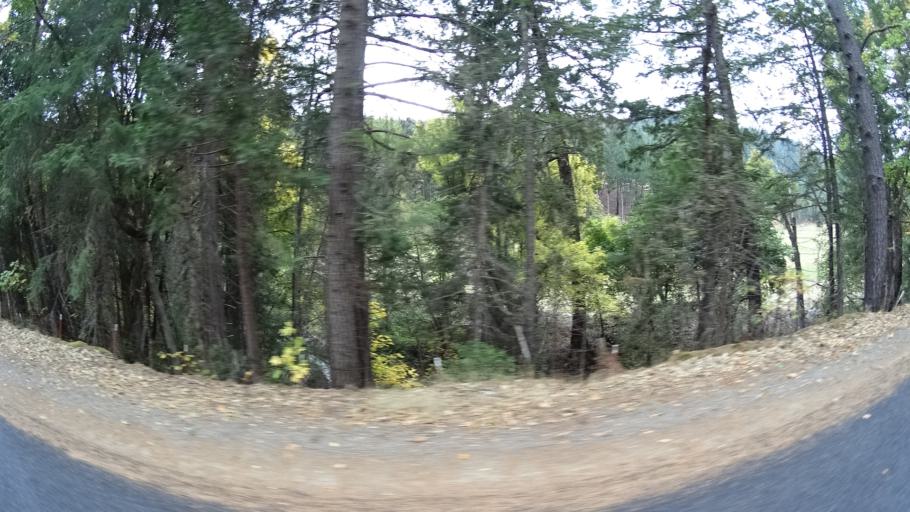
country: US
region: California
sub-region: Siskiyou County
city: Happy Camp
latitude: 41.8639
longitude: -123.1453
